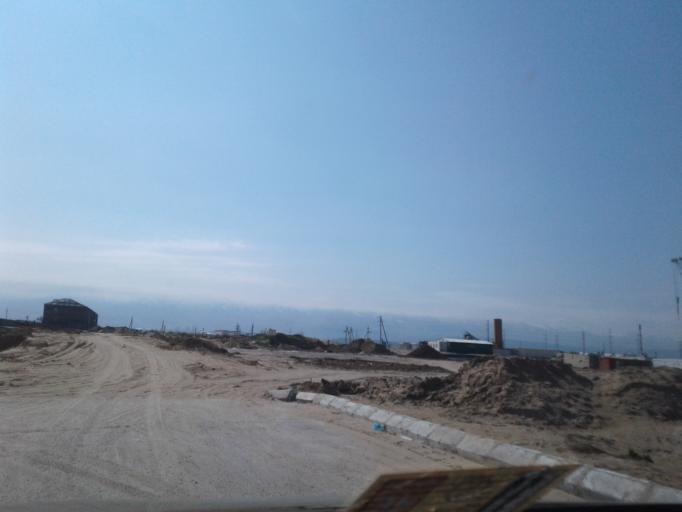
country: TM
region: Ahal
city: Ashgabat
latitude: 38.0108
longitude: 58.3930
